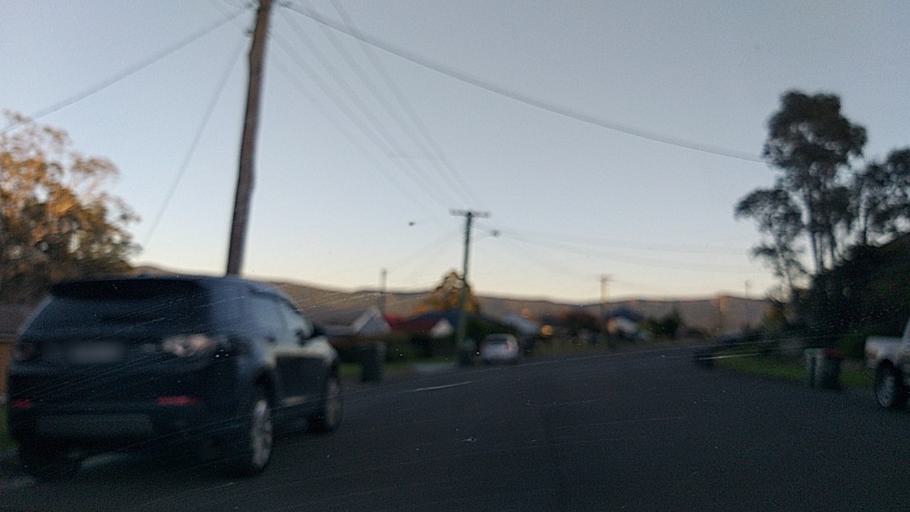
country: AU
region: New South Wales
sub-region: Wollongong
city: Dapto
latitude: -34.5086
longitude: 150.7848
